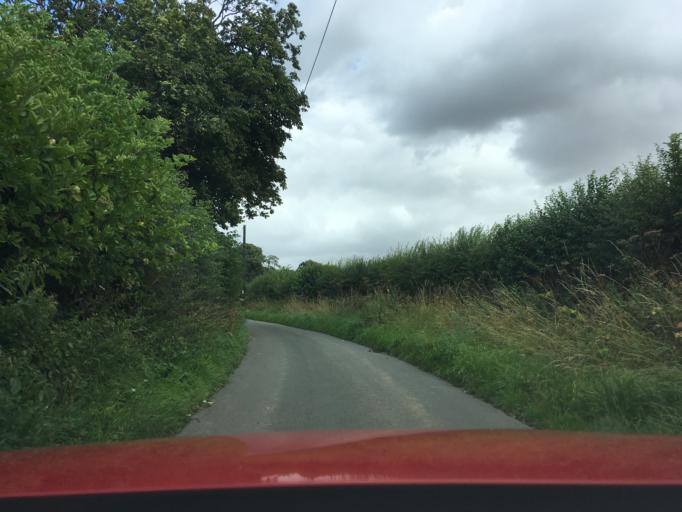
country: GB
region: England
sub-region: West Berkshire
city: Welford
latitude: 51.4153
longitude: -1.3972
